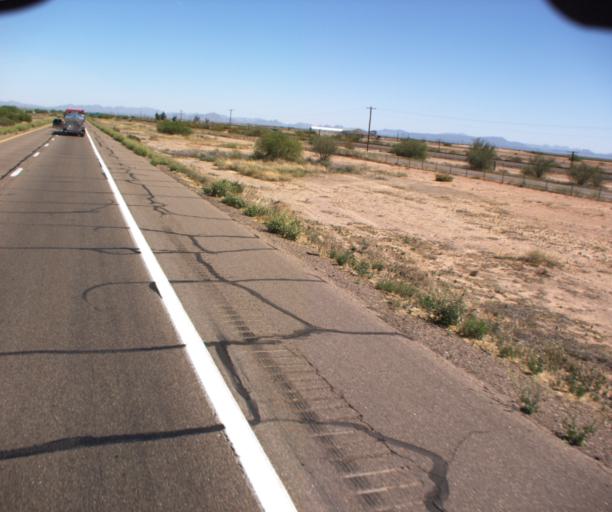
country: US
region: Arizona
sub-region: Maricopa County
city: Gila Bend
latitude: 32.9283
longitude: -112.8328
